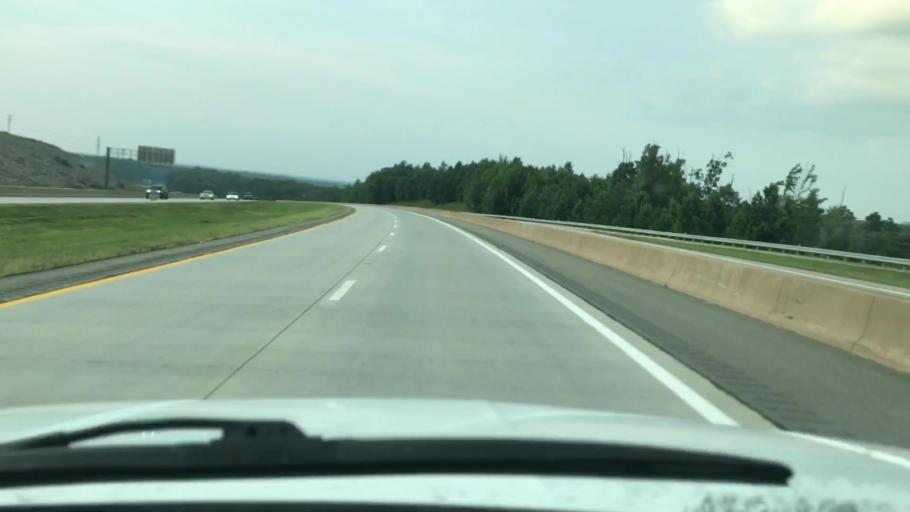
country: US
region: Virginia
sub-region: Chesterfield County
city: Brandermill
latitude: 37.5139
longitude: -77.6872
